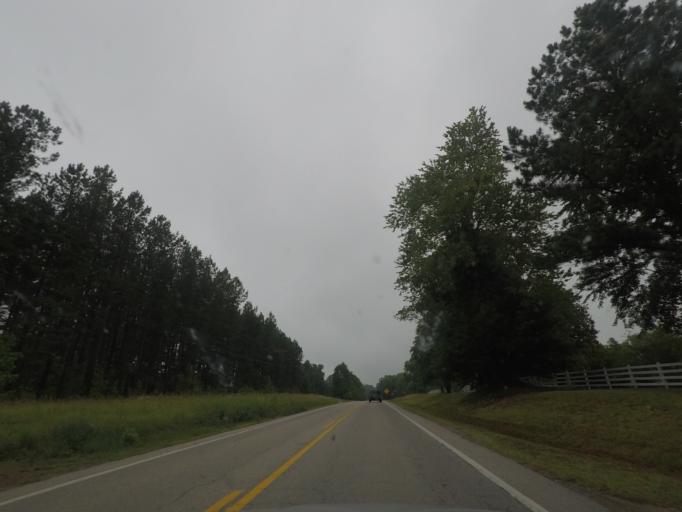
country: US
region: Virginia
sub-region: Prince Edward County
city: Hampden Sydney
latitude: 37.0921
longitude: -78.4741
